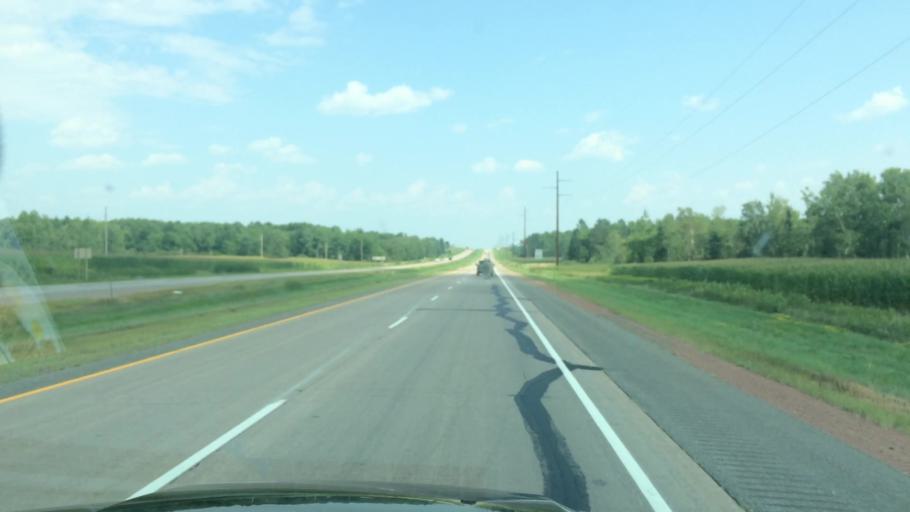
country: US
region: Wisconsin
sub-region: Marathon County
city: Edgar
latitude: 44.9441
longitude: -90.0239
